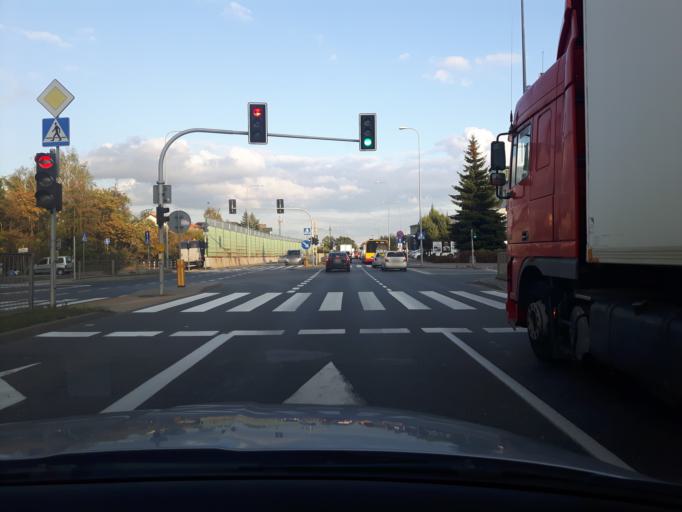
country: PL
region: Masovian Voivodeship
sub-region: Warszawa
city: Ursynow
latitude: 52.1543
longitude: 21.0100
